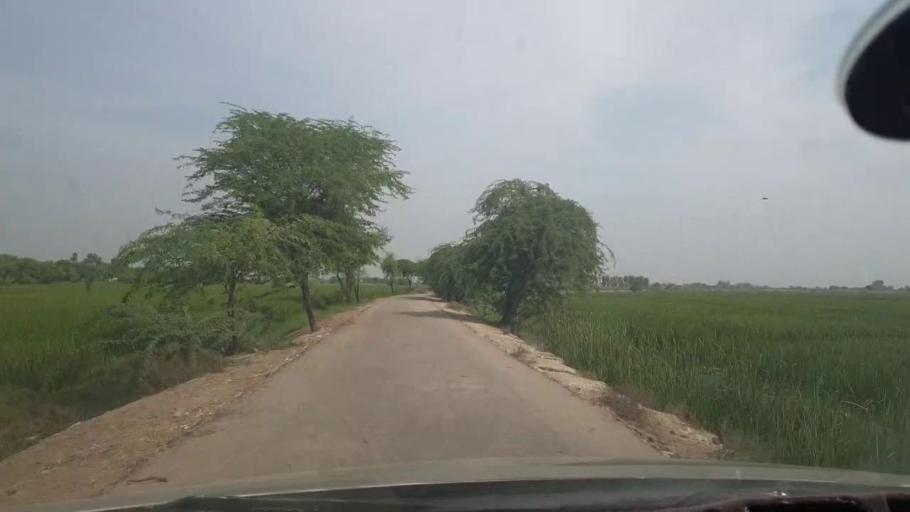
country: PK
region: Sindh
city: Jacobabad
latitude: 28.3046
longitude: 68.4748
